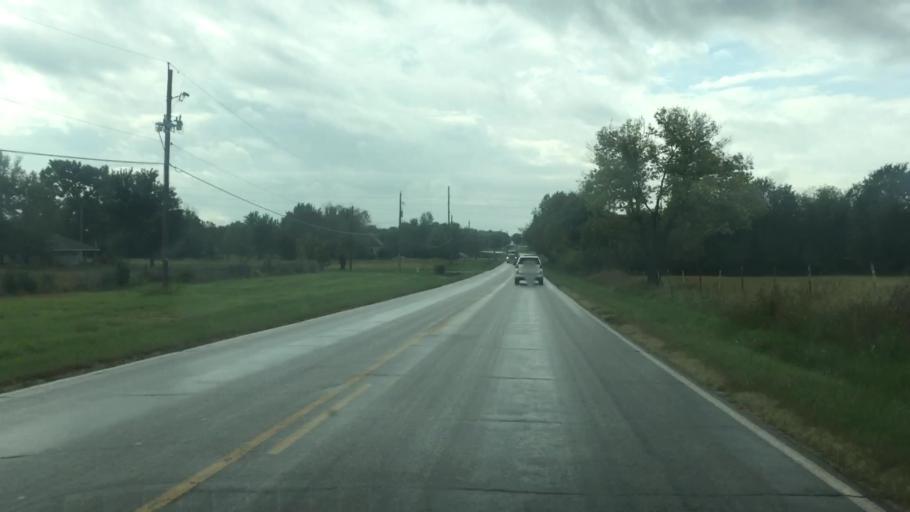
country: US
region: Kansas
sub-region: Allen County
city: Iola
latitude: 37.8956
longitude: -95.4095
